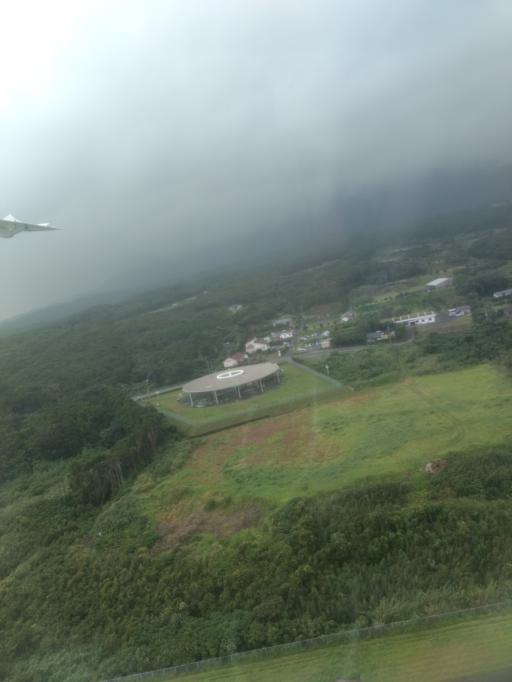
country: JP
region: Kagoshima
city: Nishinoomote
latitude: 30.3816
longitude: 130.6644
